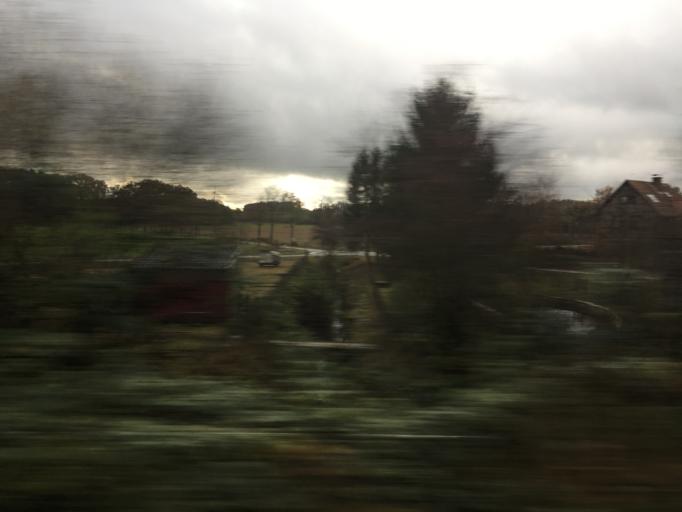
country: DE
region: North Rhine-Westphalia
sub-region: Regierungsbezirk Munster
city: Altenberge
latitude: 52.0280
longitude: 7.5405
